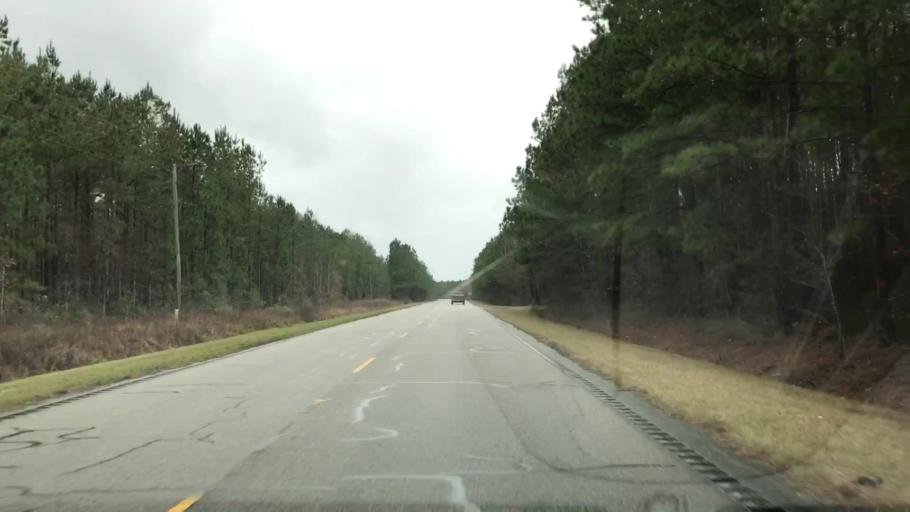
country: US
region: South Carolina
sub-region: Williamsburg County
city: Andrews
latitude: 33.5400
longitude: -79.4794
